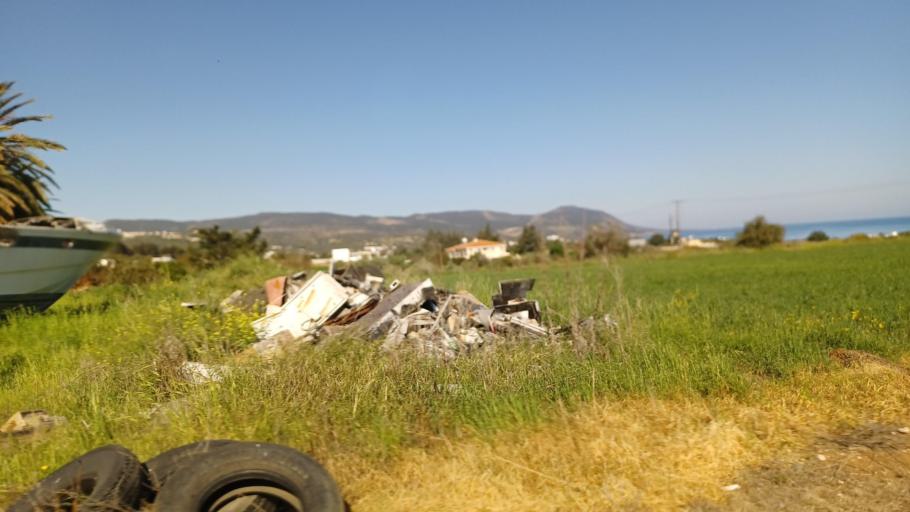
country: CY
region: Pafos
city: Polis
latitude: 35.0347
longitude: 32.3942
